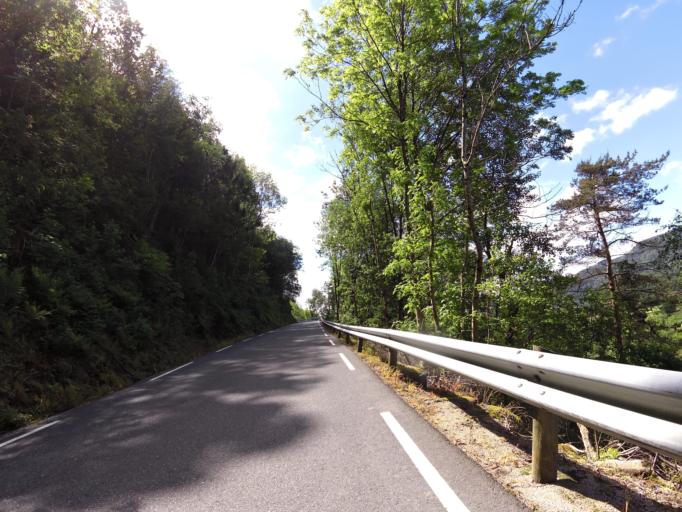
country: NO
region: Vest-Agder
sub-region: Kvinesdal
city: Liknes
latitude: 58.2996
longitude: 6.9523
